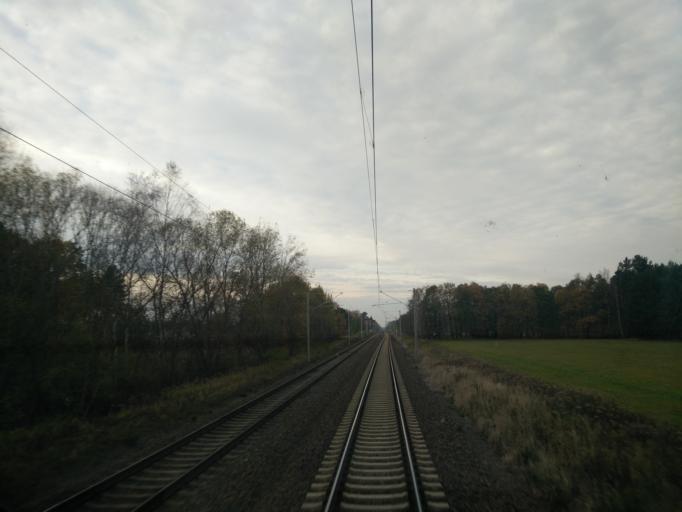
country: DE
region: Brandenburg
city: Kasel-Golzig
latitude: 51.9868
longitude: 13.7840
